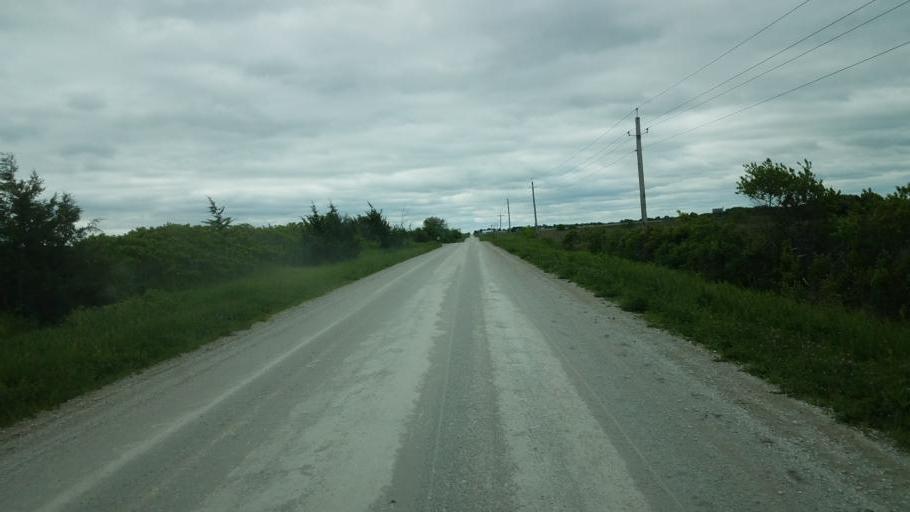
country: US
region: Iowa
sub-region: Decatur County
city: Lamoni
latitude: 40.6502
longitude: -93.9200
